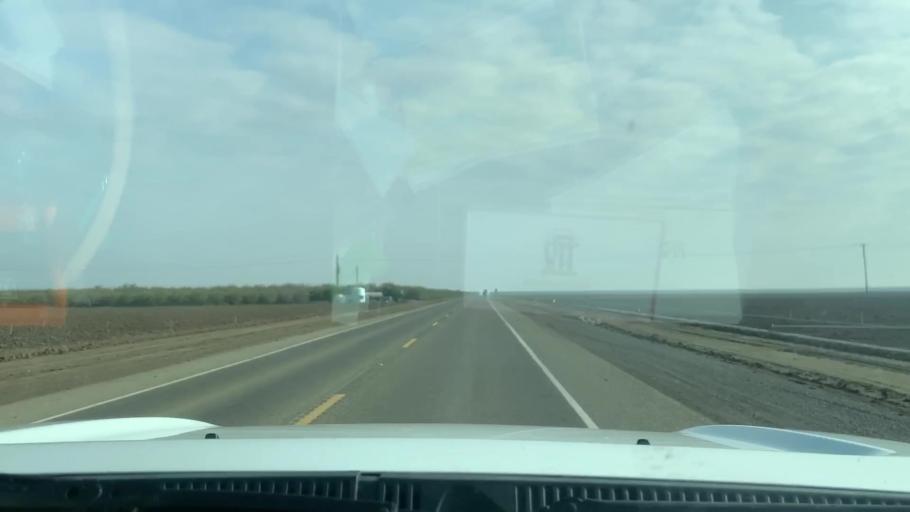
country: US
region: California
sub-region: Fresno County
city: Huron
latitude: 36.2554
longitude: -120.0695
